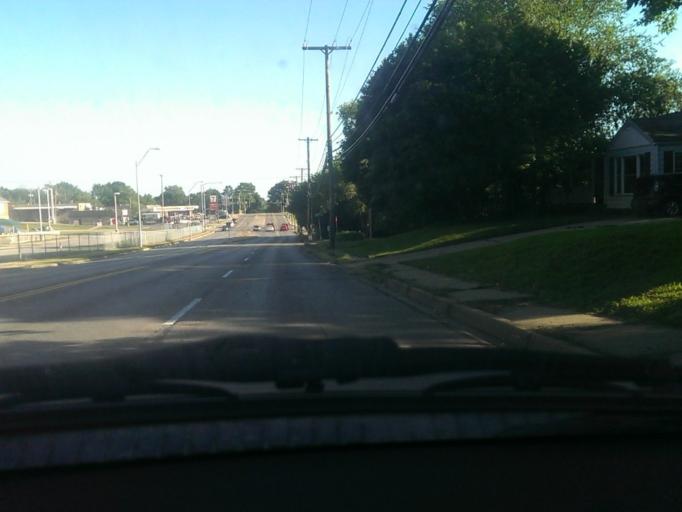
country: US
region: Kansas
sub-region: Johnson County
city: Leawood
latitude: 38.9687
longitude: -94.5954
